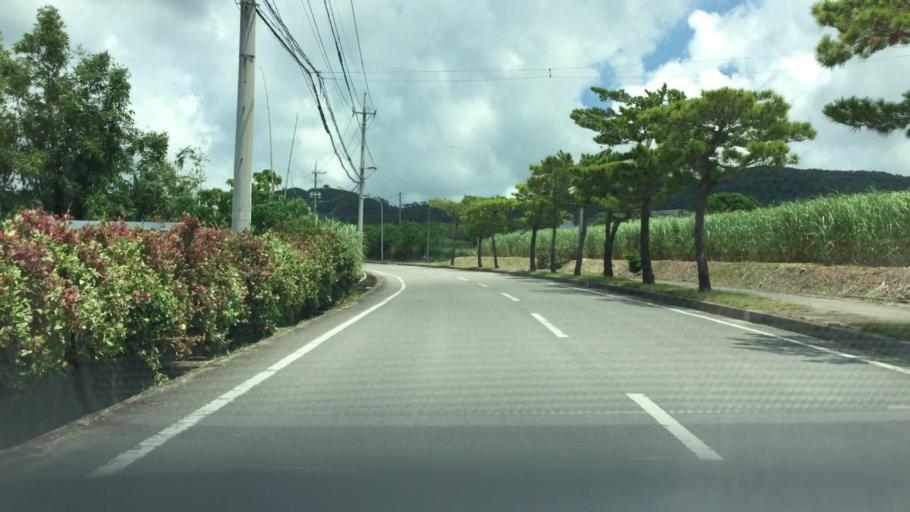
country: JP
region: Okinawa
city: Ishigaki
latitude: 24.3574
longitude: 124.1459
